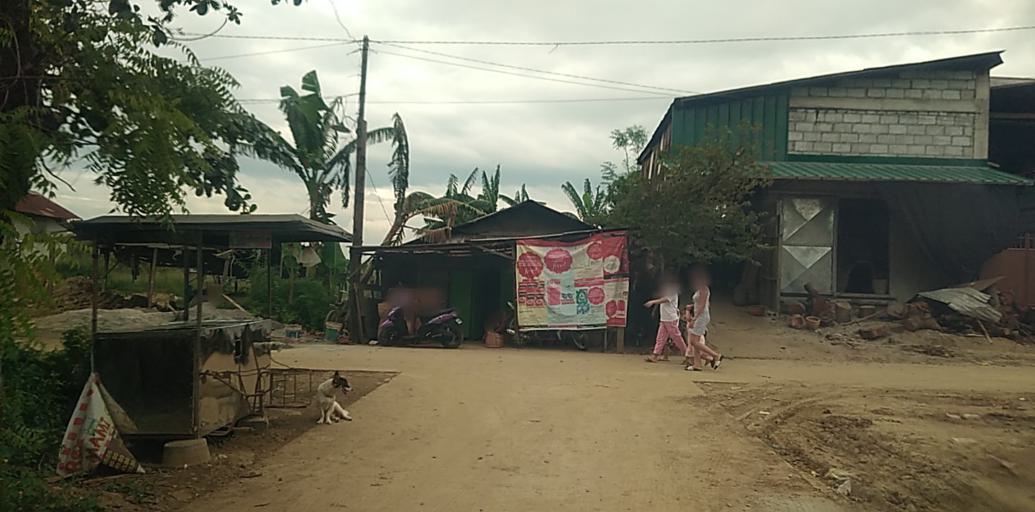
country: PH
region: Central Luzon
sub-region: Province of Pampanga
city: San Fernando
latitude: 15.0060
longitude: 120.7053
